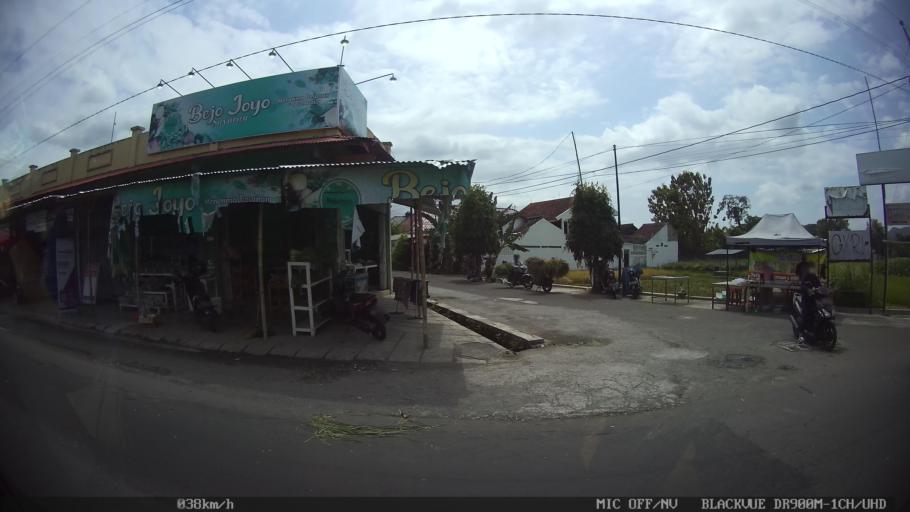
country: ID
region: Central Java
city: Candi Prambanan
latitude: -7.7735
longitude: 110.4709
